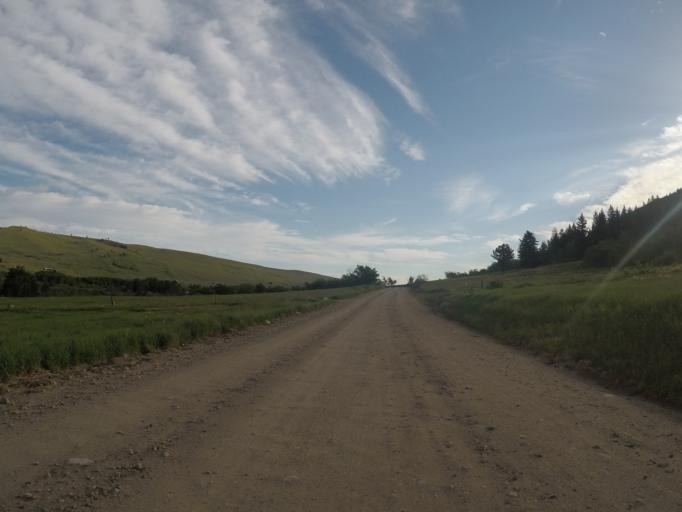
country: US
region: Montana
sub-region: Stillwater County
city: Absarokee
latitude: 45.2772
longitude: -109.5496
